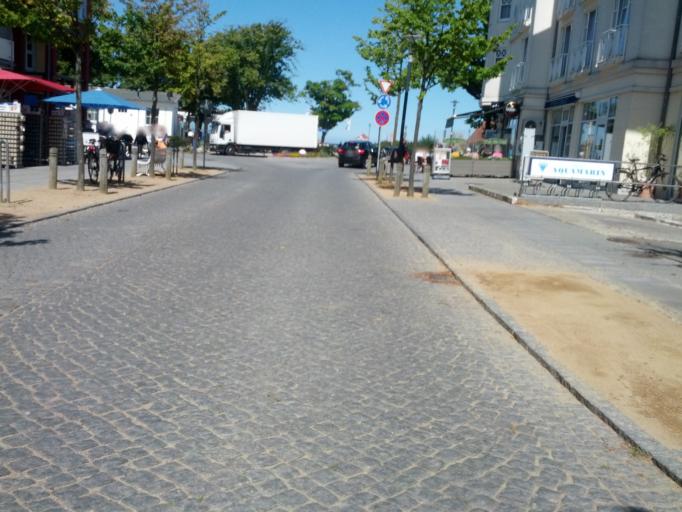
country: DE
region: Mecklenburg-Vorpommern
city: Ostseebad Kuhlungsborn
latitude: 54.1517
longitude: 11.7338
